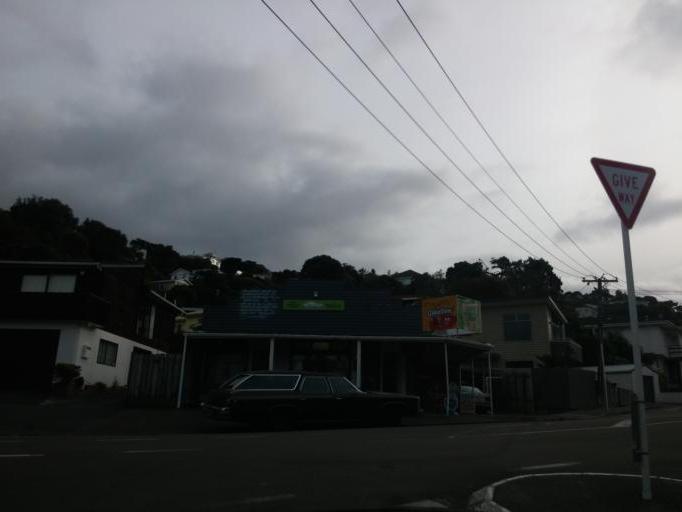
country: NZ
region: Wellington
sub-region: Wellington City
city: Brooklyn
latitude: -41.3129
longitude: 174.7702
